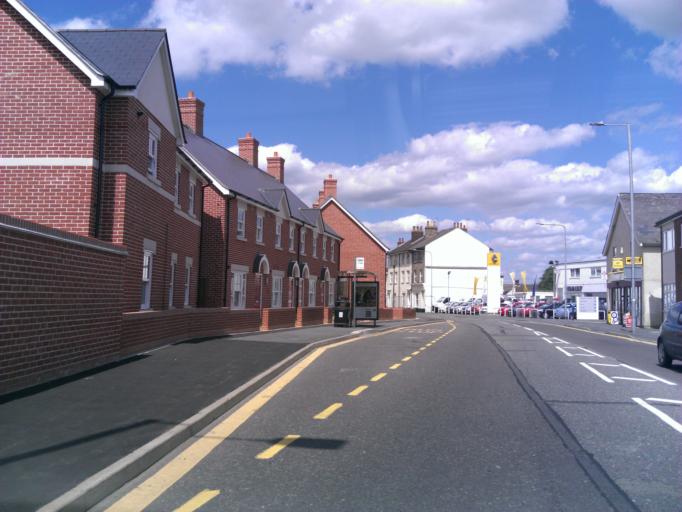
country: GB
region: England
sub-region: Essex
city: Colchester
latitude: 51.8821
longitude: 0.9096
